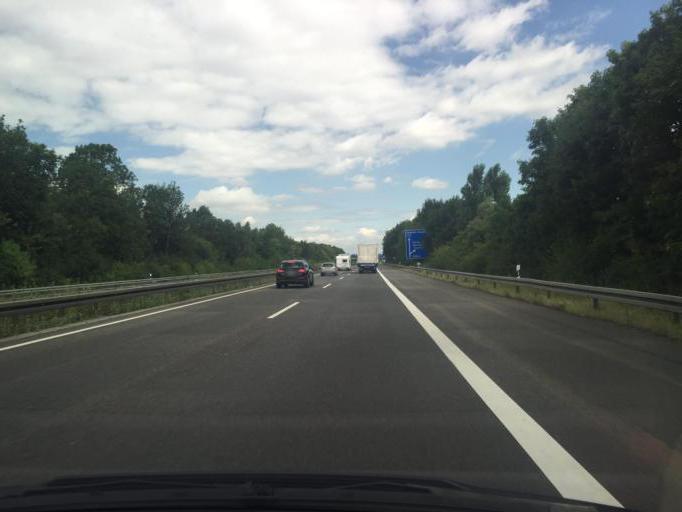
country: DE
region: Hesse
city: Zwingenberg
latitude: 49.7163
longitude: 8.5957
